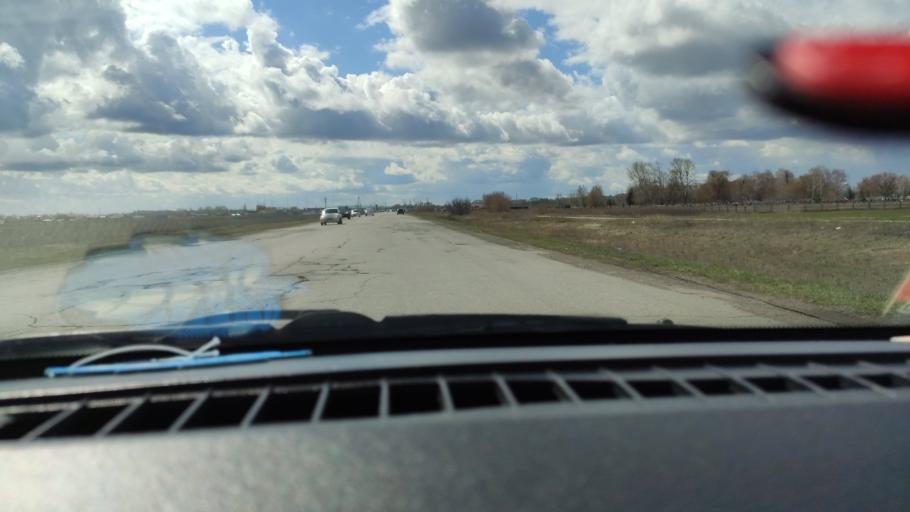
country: RU
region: Samara
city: Tol'yatti
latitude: 53.6815
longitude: 49.4159
